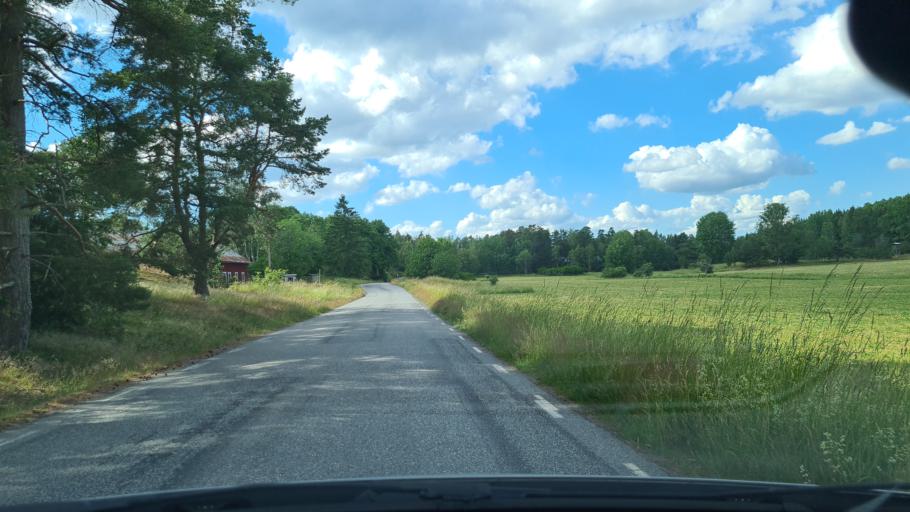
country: SE
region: Stockholm
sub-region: Varmdo Kommun
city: Mortnas
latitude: 59.4070
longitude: 18.4565
